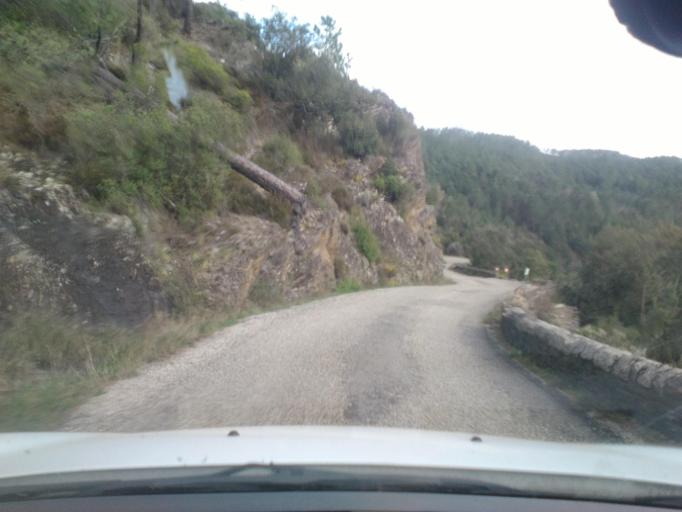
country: FR
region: Languedoc-Roussillon
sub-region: Departement du Gard
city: Lasalle
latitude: 44.1305
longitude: 3.7605
